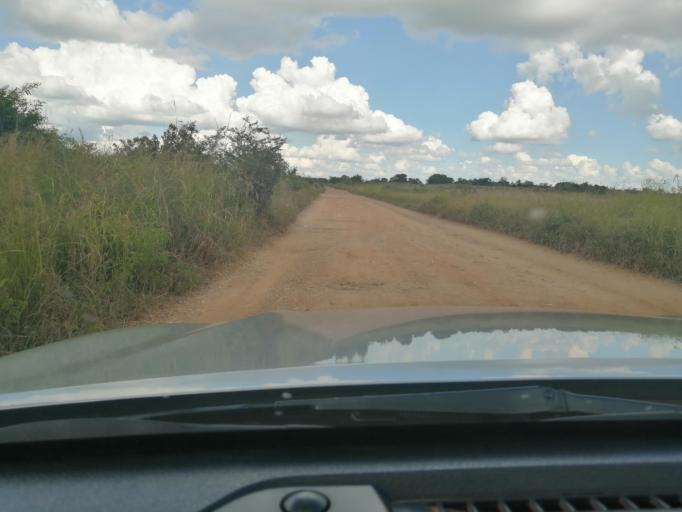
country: ZM
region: Lusaka
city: Lusaka
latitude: -15.2104
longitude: 28.0911
